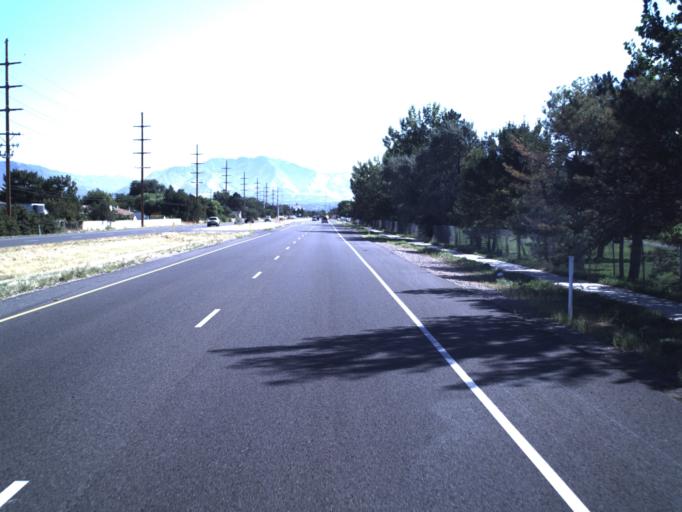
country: US
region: Utah
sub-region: Salt Lake County
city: Taylorsville
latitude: 40.6684
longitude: -111.9323
